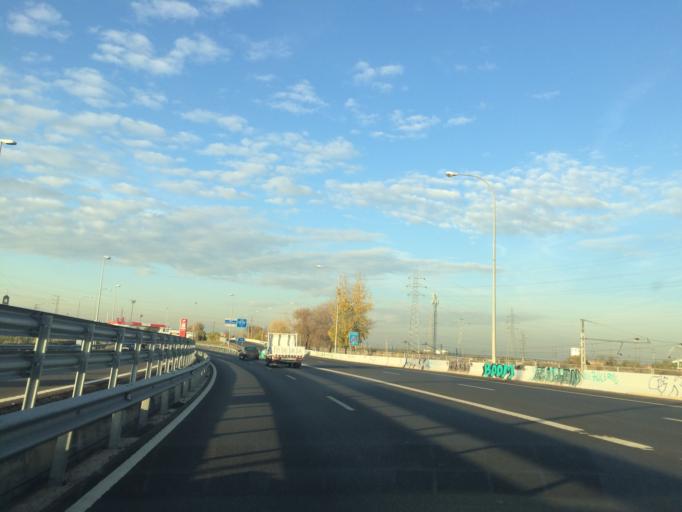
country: ES
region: Madrid
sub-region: Provincia de Madrid
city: Las Tablas
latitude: 40.5136
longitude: -3.6846
